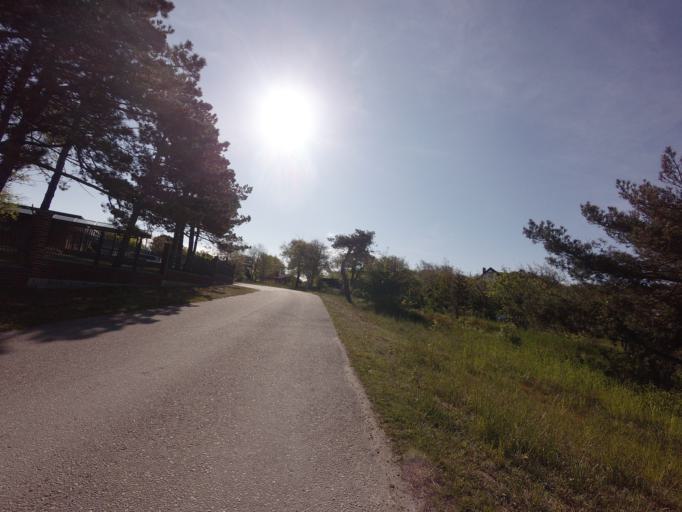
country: SE
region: Skane
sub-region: Hoganas Kommun
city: Hoganas
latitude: 56.2291
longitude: 12.5406
